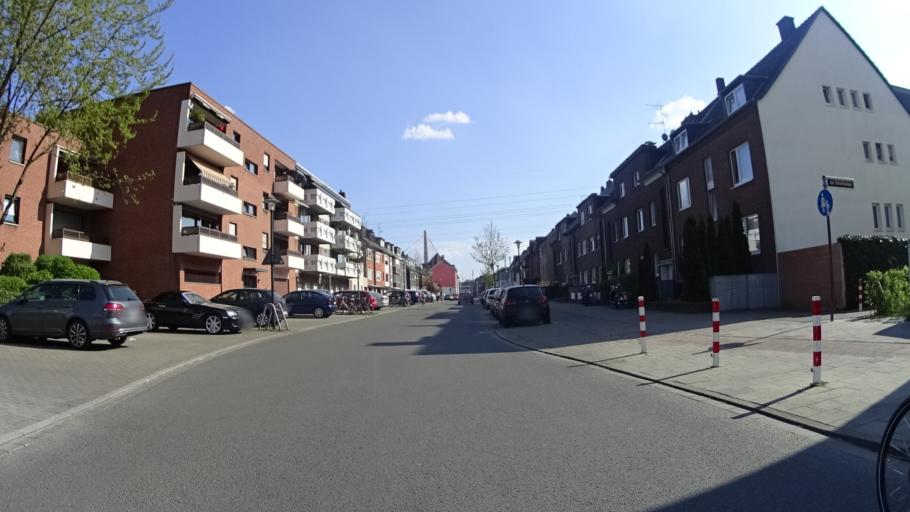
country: DE
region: North Rhine-Westphalia
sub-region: Regierungsbezirk Dusseldorf
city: Dusseldorf
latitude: 51.1935
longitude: 6.7699
